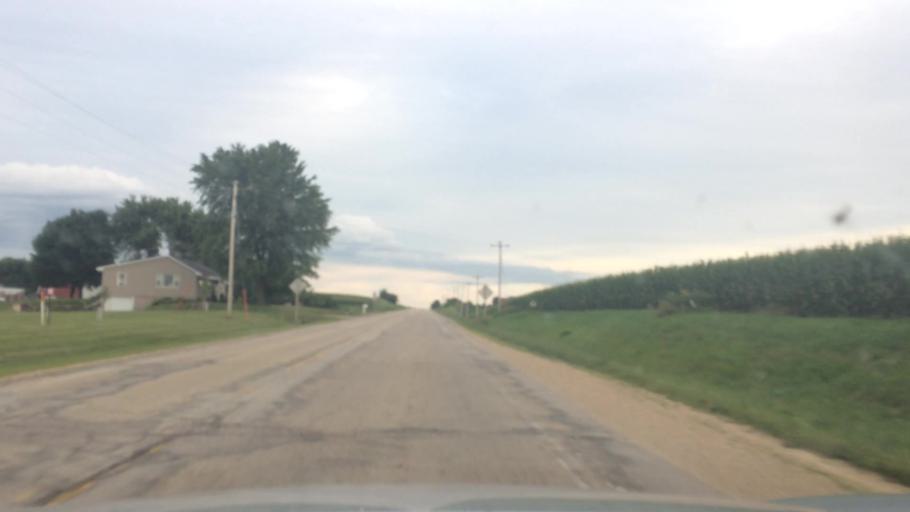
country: US
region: Wisconsin
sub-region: Columbia County
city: Lodi
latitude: 43.2497
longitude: -89.5211
